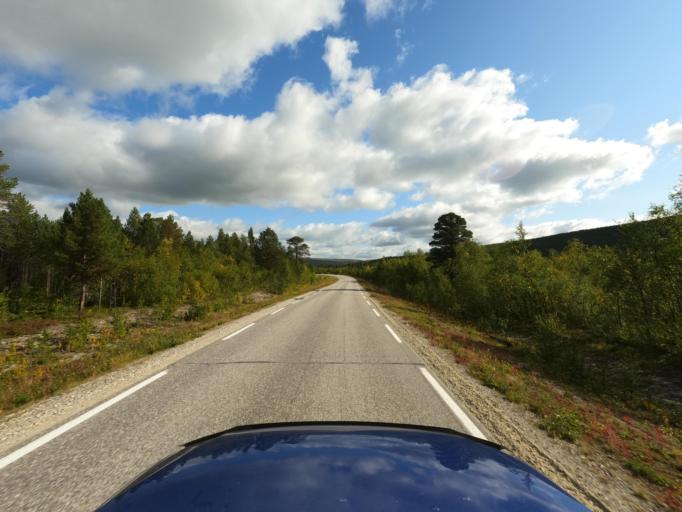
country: NO
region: Finnmark Fylke
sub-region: Karasjok
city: Karasjohka
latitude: 69.4311
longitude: 24.9609
